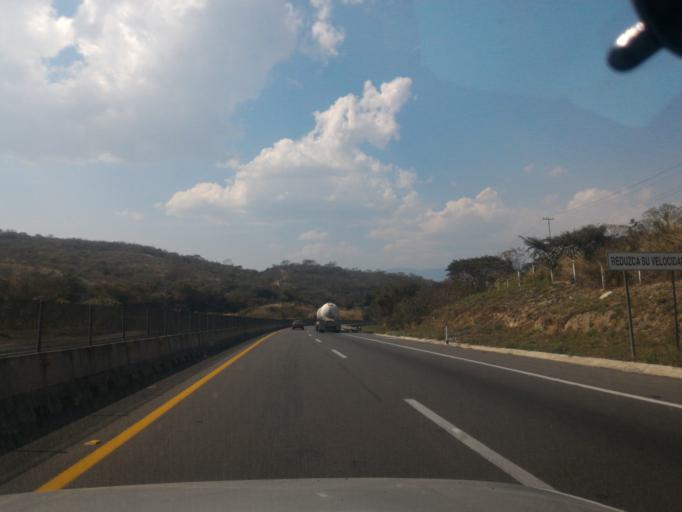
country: MX
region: Jalisco
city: San Andres Ixtlan
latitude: 19.8430
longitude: -103.5037
